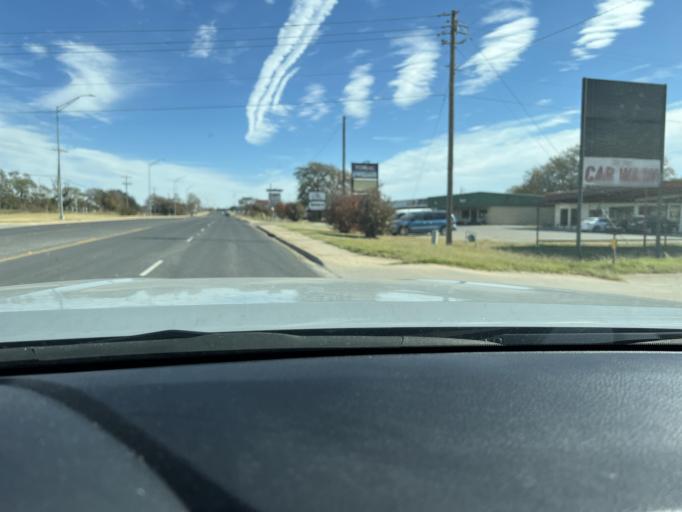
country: US
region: Texas
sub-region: Eastland County
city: Eastland
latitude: 32.4017
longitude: -98.8054
